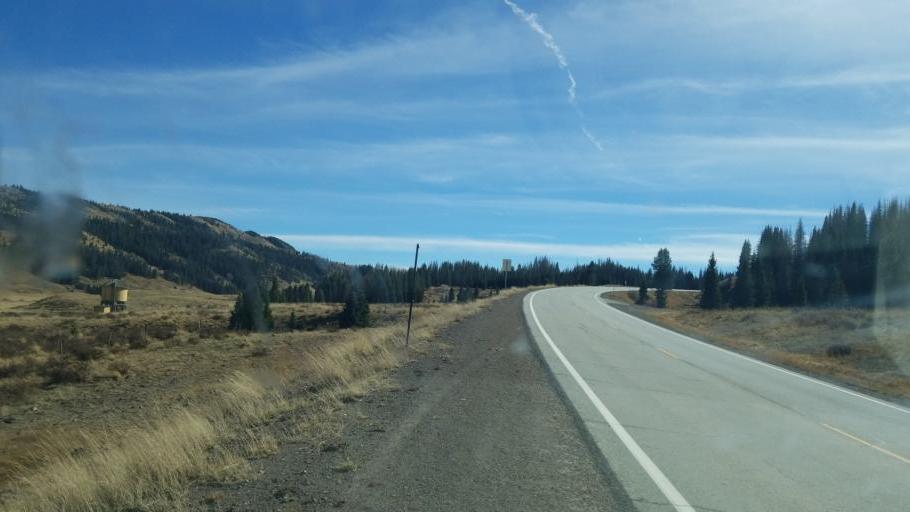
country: US
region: New Mexico
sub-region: Rio Arriba County
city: Chama
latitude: 37.0420
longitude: -106.4106
